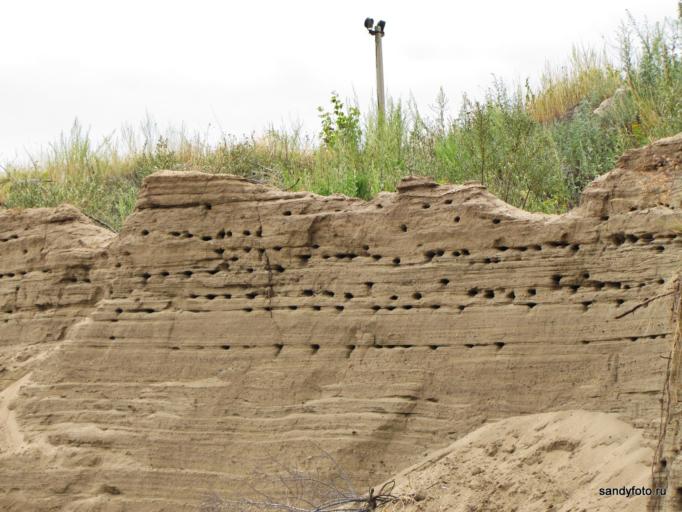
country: RU
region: Chelyabinsk
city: Troitsk
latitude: 54.0656
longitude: 61.5877
